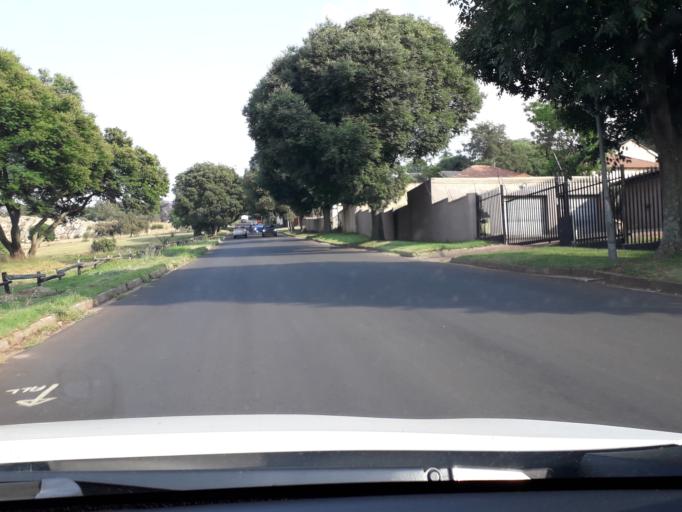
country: ZA
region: Gauteng
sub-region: City of Johannesburg Metropolitan Municipality
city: Johannesburg
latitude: -26.1561
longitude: 27.9725
